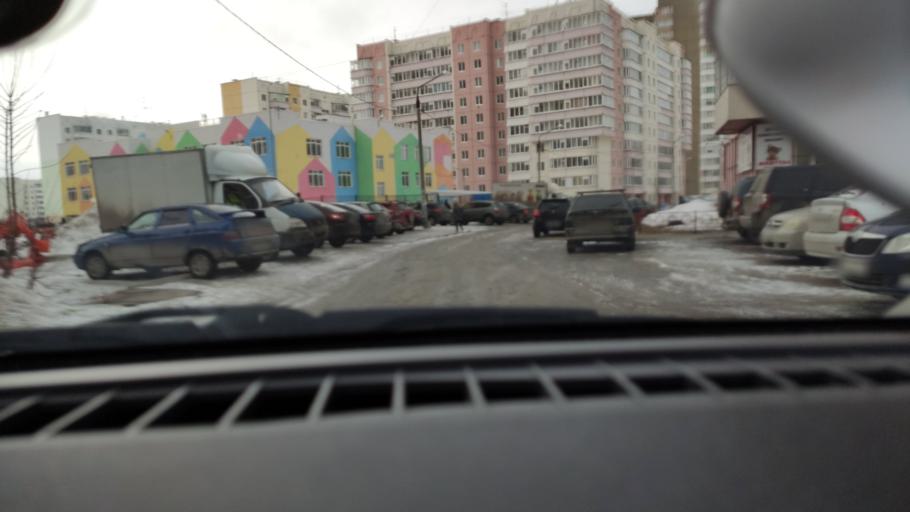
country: RU
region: Perm
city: Polazna
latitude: 58.1337
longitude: 56.4010
